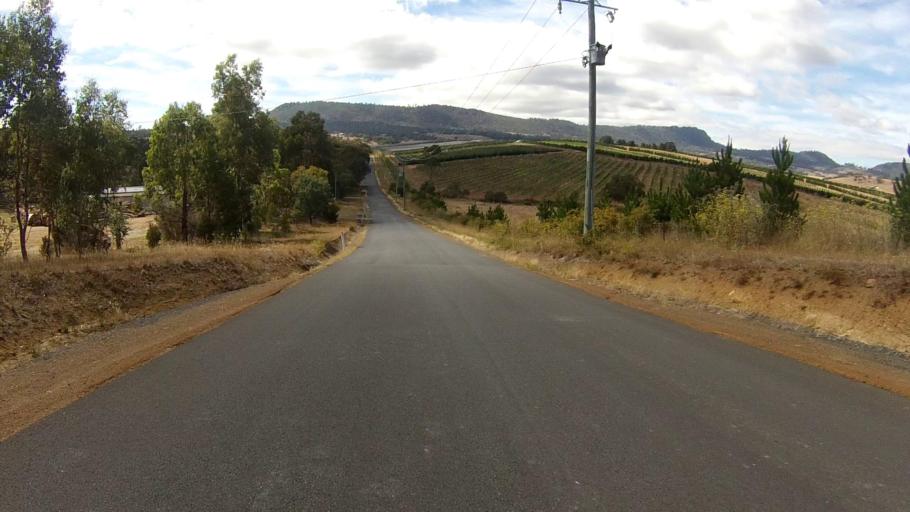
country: AU
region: Tasmania
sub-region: Brighton
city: Old Beach
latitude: -42.7368
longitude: 147.2890
